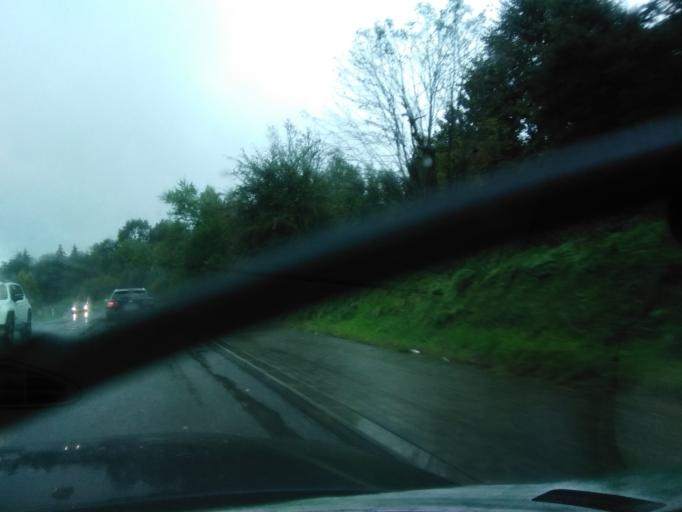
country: PL
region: Subcarpathian Voivodeship
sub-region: Powiat ropczycko-sedziszowski
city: Niedzwiada
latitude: 50.0129
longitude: 21.5521
